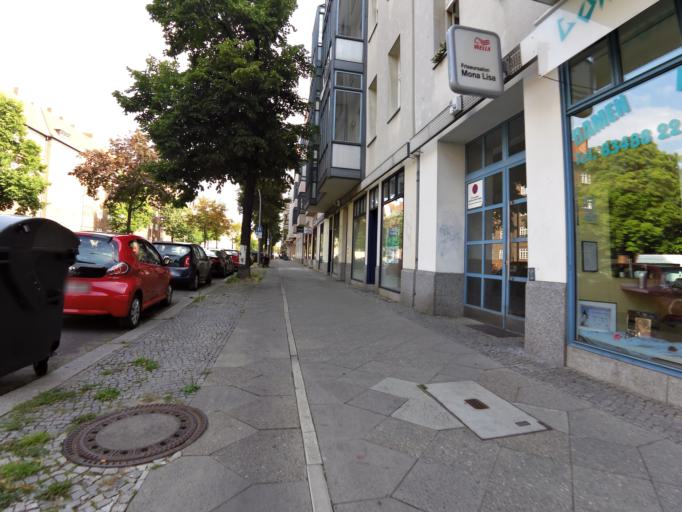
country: DE
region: Berlin
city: Lichterfelde
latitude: 52.4454
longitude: 13.3153
